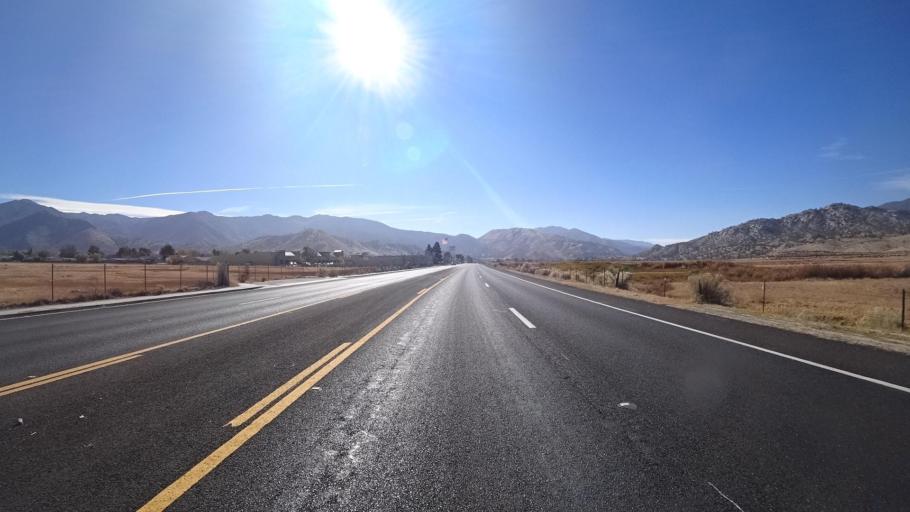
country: US
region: California
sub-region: Kern County
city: Lake Isabella
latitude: 35.6203
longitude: -118.4780
